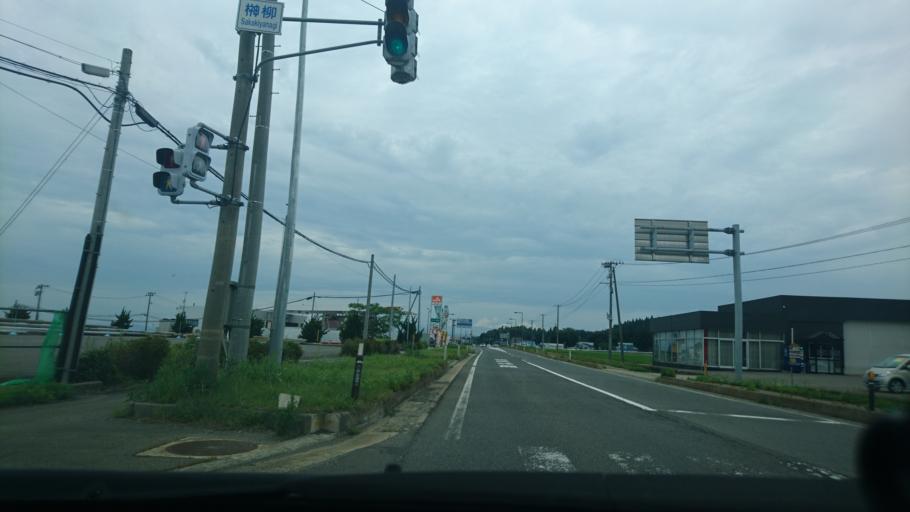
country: JP
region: Akita
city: Yokotemachi
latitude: 39.3775
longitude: 140.5682
